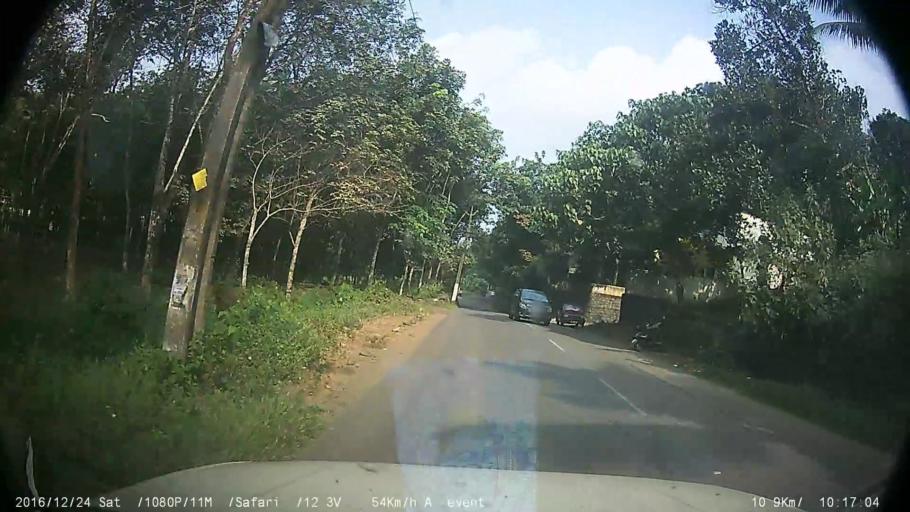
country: IN
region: Kerala
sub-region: Kottayam
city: Palackattumala
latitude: 9.8211
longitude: 76.6086
